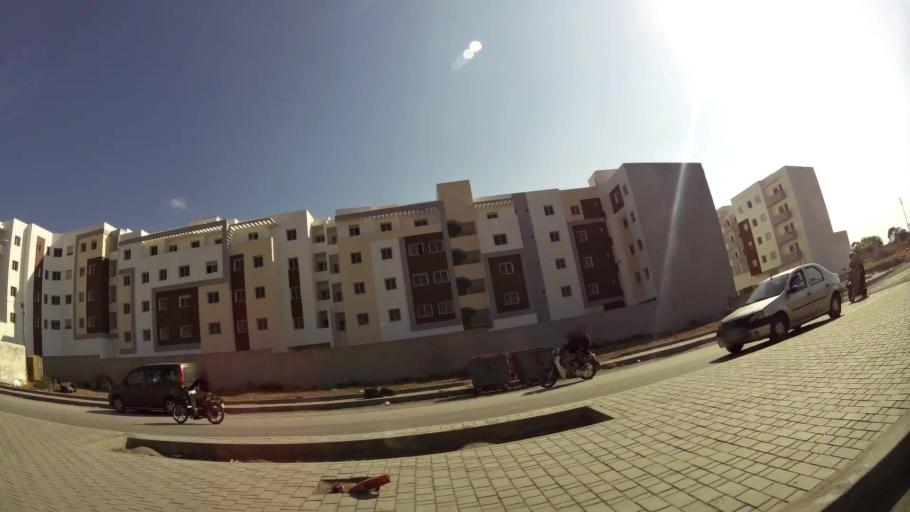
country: MA
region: Rabat-Sale-Zemmour-Zaer
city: Sale
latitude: 34.0572
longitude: -6.7979
